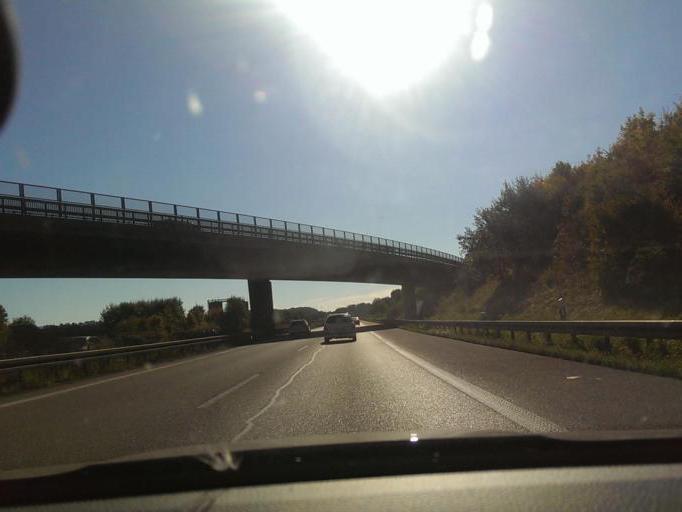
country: DE
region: Baden-Wuerttemberg
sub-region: Regierungsbezirk Stuttgart
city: Leonberg
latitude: 48.7809
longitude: 9.0133
